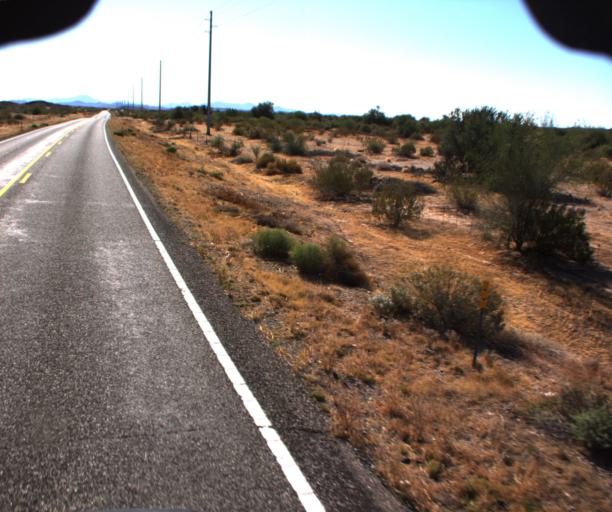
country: US
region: Arizona
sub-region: La Paz County
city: Cienega Springs
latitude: 33.9937
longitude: -114.0934
